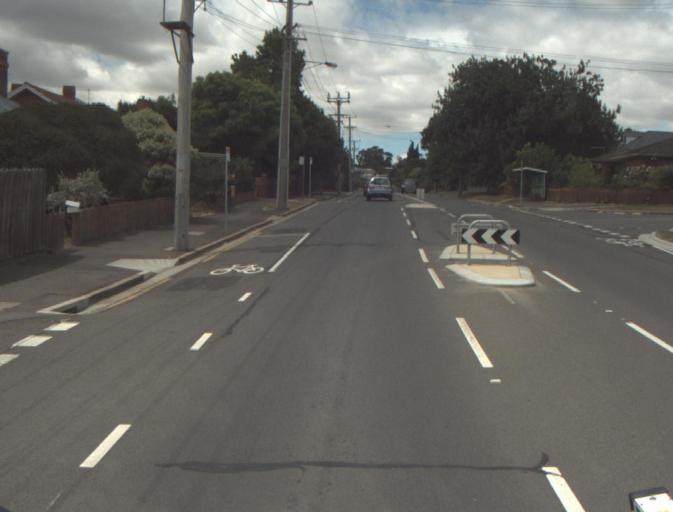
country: AU
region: Tasmania
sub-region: Launceston
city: Newstead
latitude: -41.4435
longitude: 147.1619
